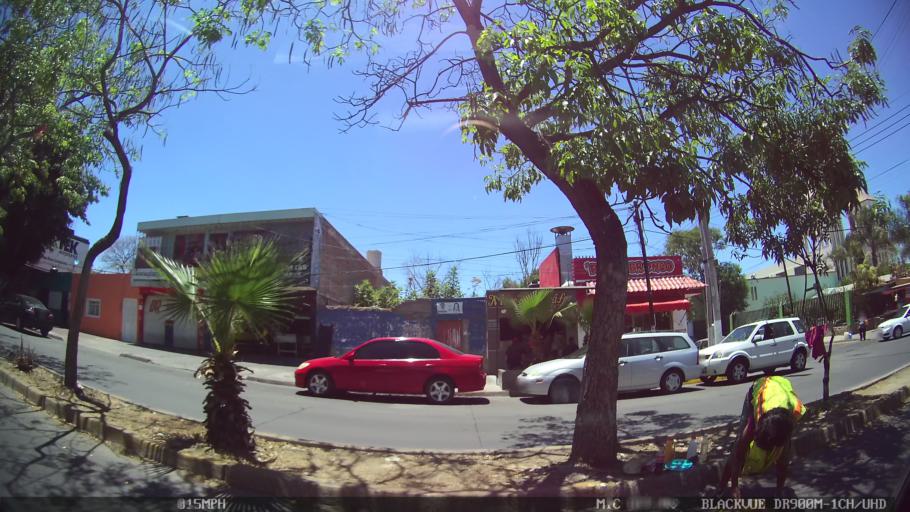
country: MX
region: Jalisco
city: Tlaquepaque
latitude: 20.6713
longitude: -103.2777
